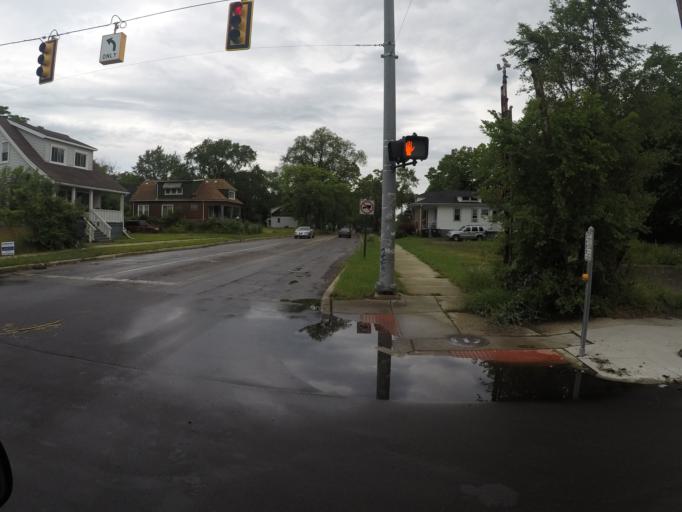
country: US
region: Michigan
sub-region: Wayne County
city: Grosse Pointe Park
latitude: 42.3849
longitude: -82.9906
